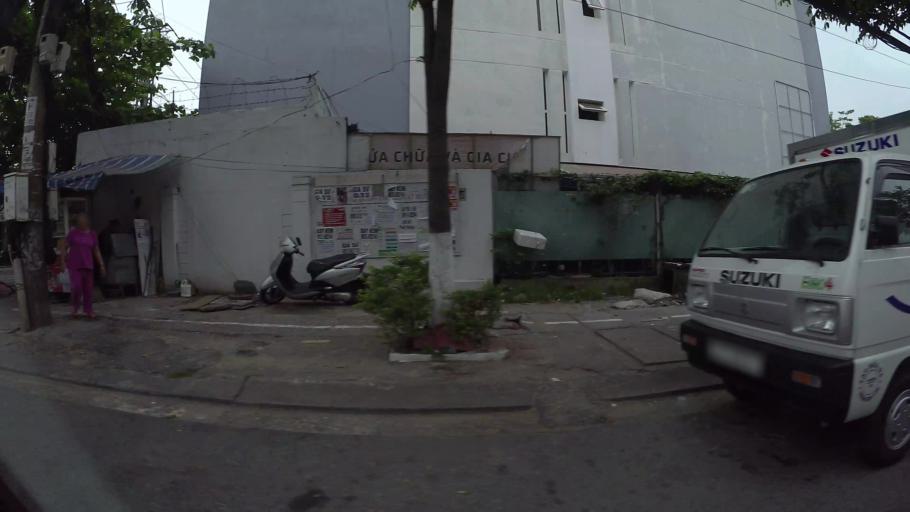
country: VN
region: Da Nang
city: Cam Le
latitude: 16.0322
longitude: 108.2228
